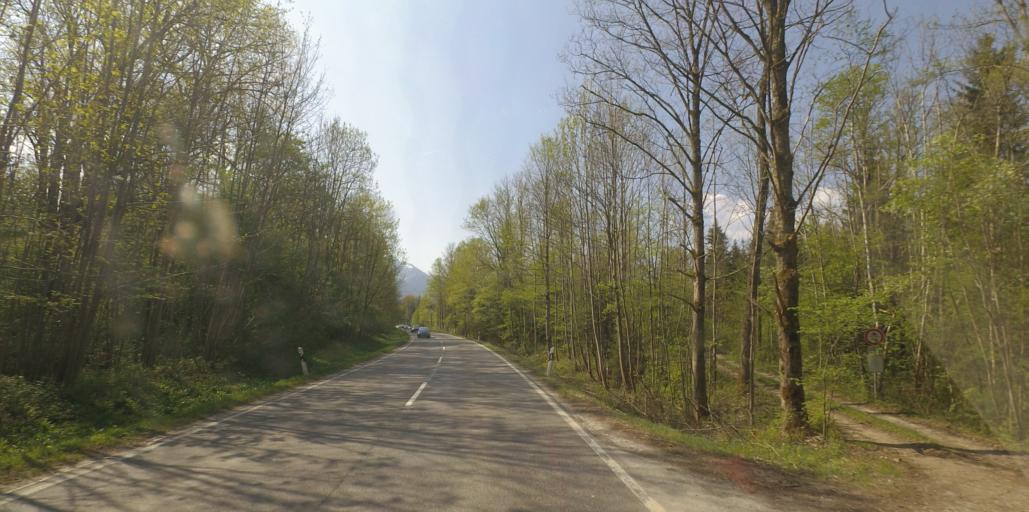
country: DE
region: Bavaria
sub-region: Upper Bavaria
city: Ubersee
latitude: 47.8255
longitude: 12.5114
